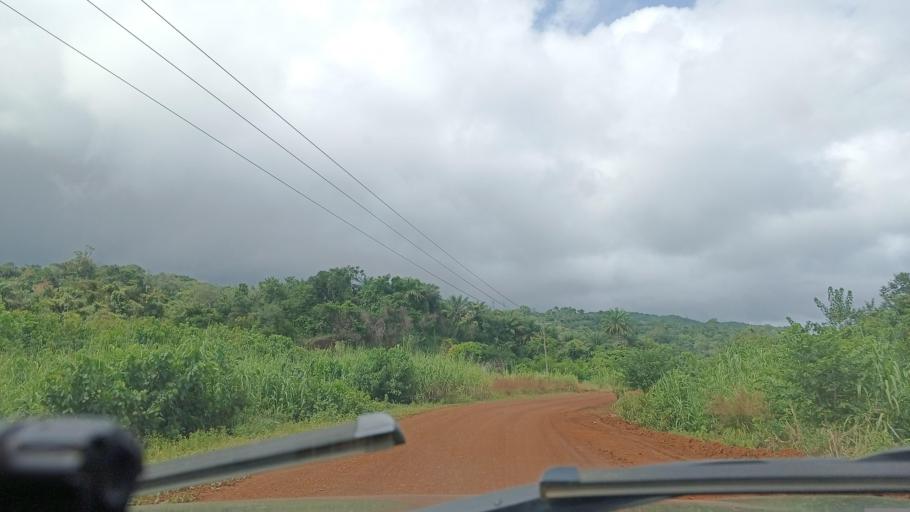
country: LR
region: Grand Cape Mount
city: Robertsport
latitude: 6.7469
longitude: -11.3508
